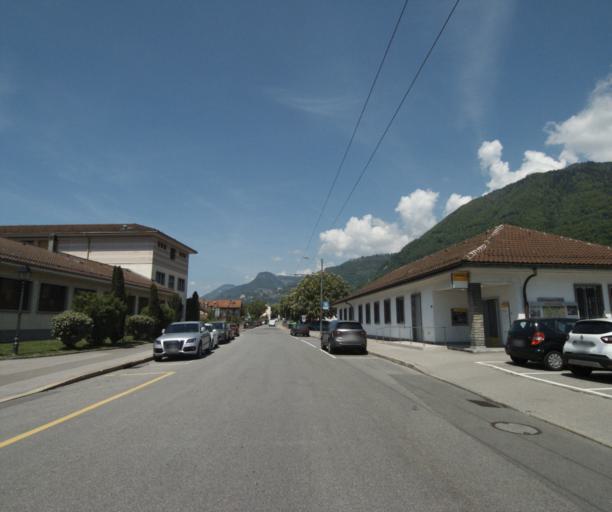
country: CH
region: Vaud
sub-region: Aigle District
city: Villeneuve
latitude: 46.3989
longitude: 6.9263
